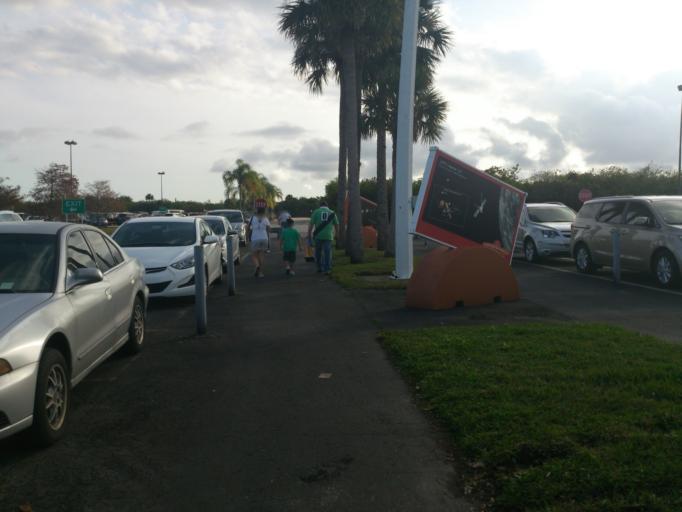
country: US
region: Florida
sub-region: Brevard County
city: Merritt Island
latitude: 28.5206
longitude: -80.6819
